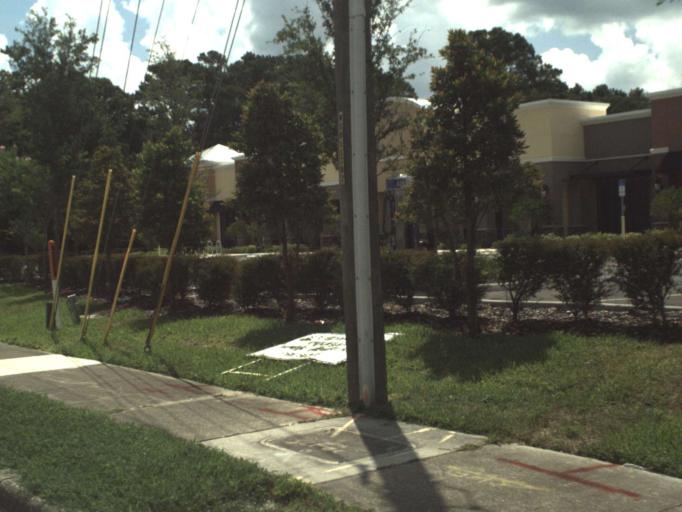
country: US
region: Florida
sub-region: Seminole County
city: Winter Springs
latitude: 28.7009
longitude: -81.2969
